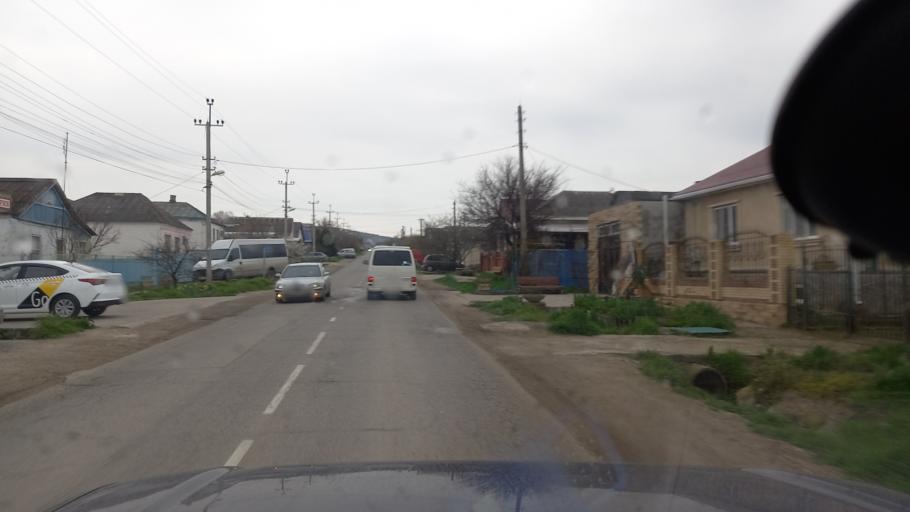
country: RU
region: Krasnodarskiy
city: Sukko
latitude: 44.8593
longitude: 37.4374
